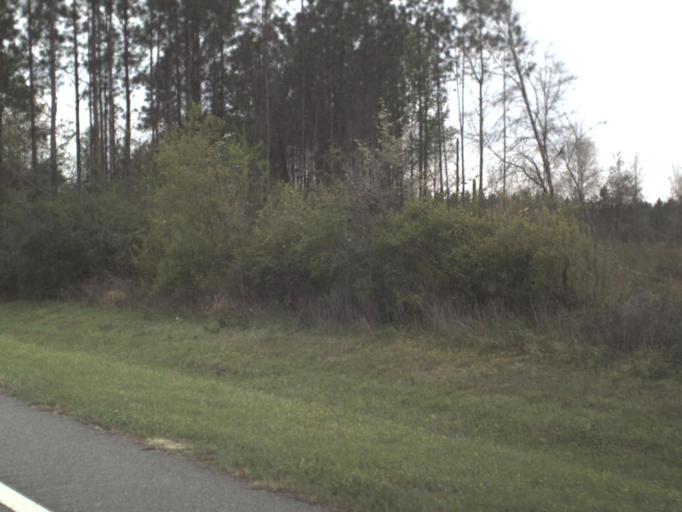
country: US
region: Florida
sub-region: Gulf County
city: Wewahitchka
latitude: 30.2530
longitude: -85.2311
